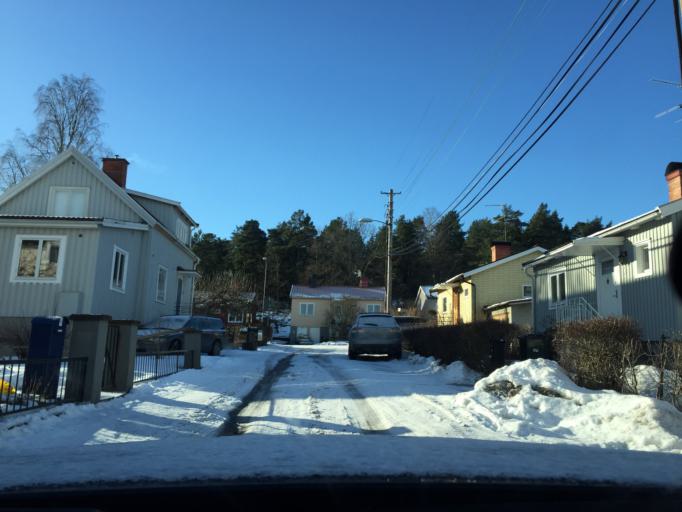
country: SE
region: Stockholm
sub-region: Stockholms Kommun
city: Bromma
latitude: 59.3531
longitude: 17.8980
